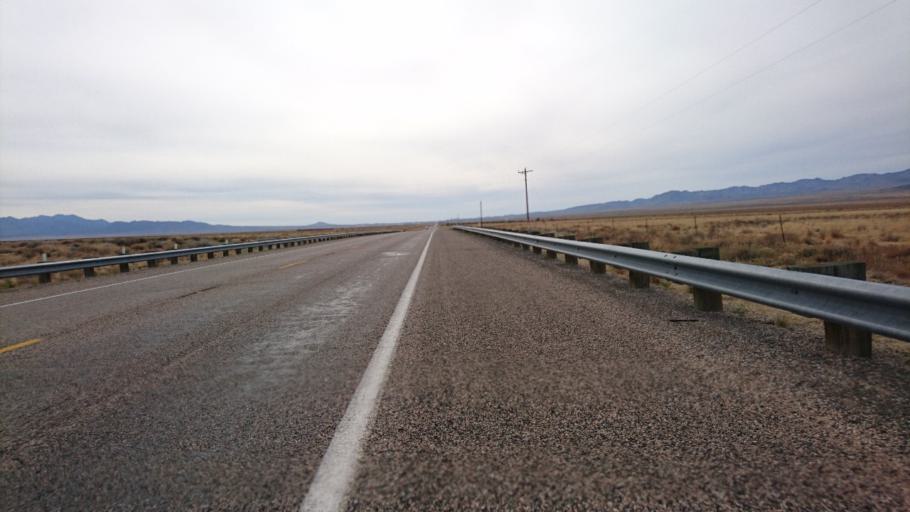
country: US
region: Arizona
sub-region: Mohave County
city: New Kingman-Butler
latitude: 35.3627
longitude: -113.8715
